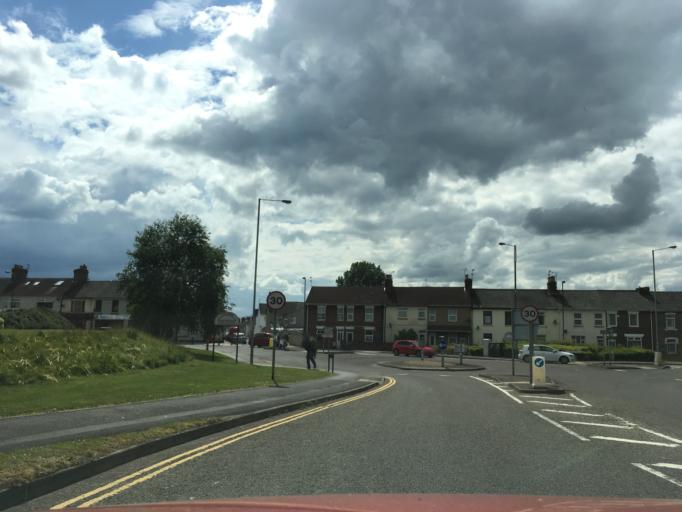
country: GB
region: England
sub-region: Borough of Swindon
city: Swindon
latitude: 51.5638
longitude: -1.7991
